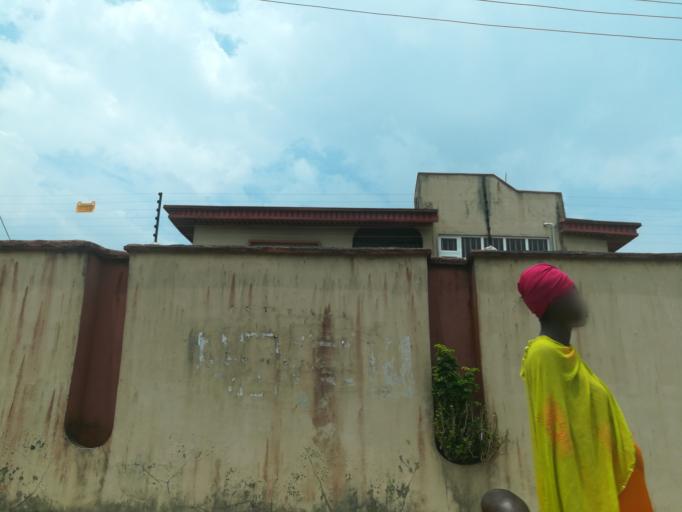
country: NG
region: Lagos
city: Ikorodu
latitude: 6.5707
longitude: 3.5926
